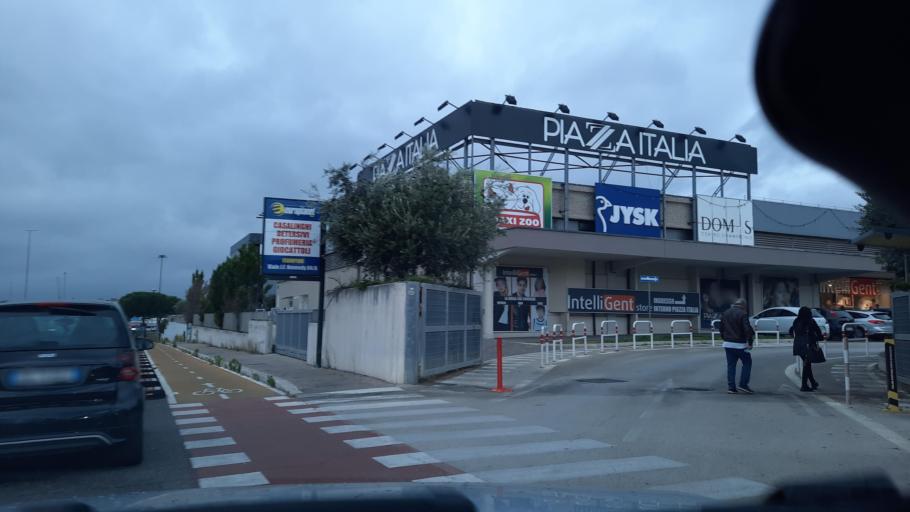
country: IT
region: Latium
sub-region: Citta metropolitana di Roma Capitale
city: Ciampino
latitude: 41.8463
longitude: 12.6077
